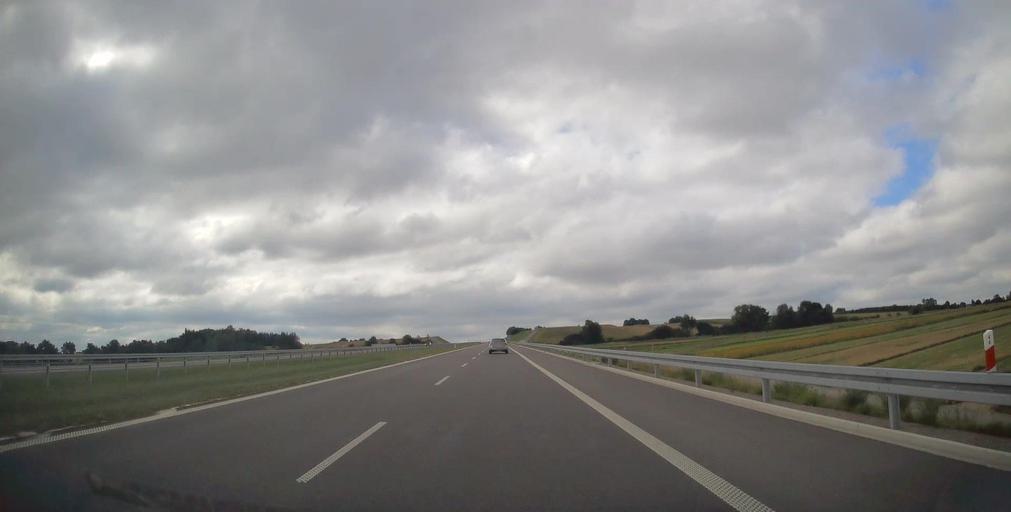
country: PL
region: Lesser Poland Voivodeship
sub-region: Powiat krakowski
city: Slomniki
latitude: 50.2795
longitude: 20.0217
